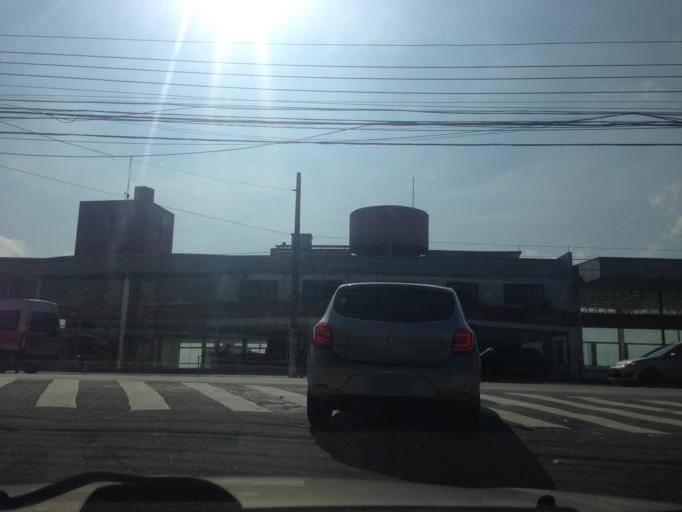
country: BR
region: Sao Paulo
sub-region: Sao Paulo
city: Sao Paulo
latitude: -23.5391
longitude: -46.7075
